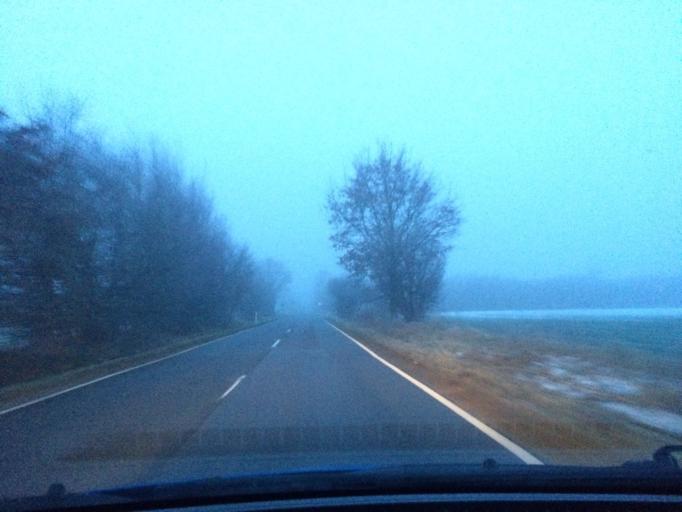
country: DE
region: Schleswig-Holstein
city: Wiershop
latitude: 53.4472
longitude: 10.4513
